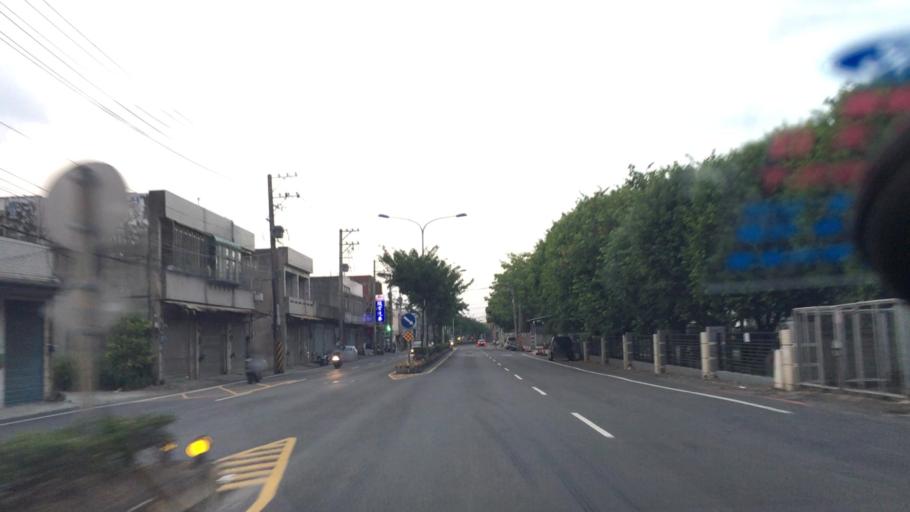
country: TW
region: Taiwan
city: Taoyuan City
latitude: 25.0580
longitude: 121.2679
